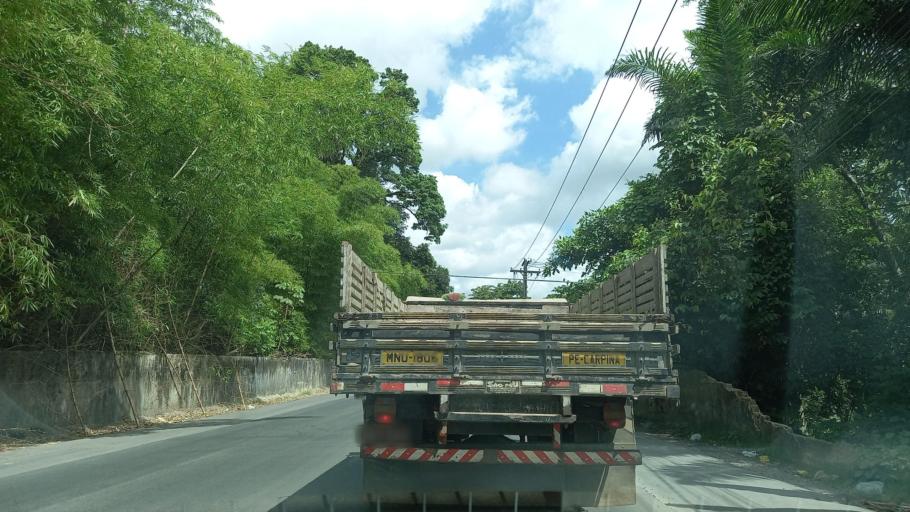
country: BR
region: Pernambuco
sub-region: Jaboatao Dos Guararapes
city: Jaboatao dos Guararapes
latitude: -8.1133
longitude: -35.0072
